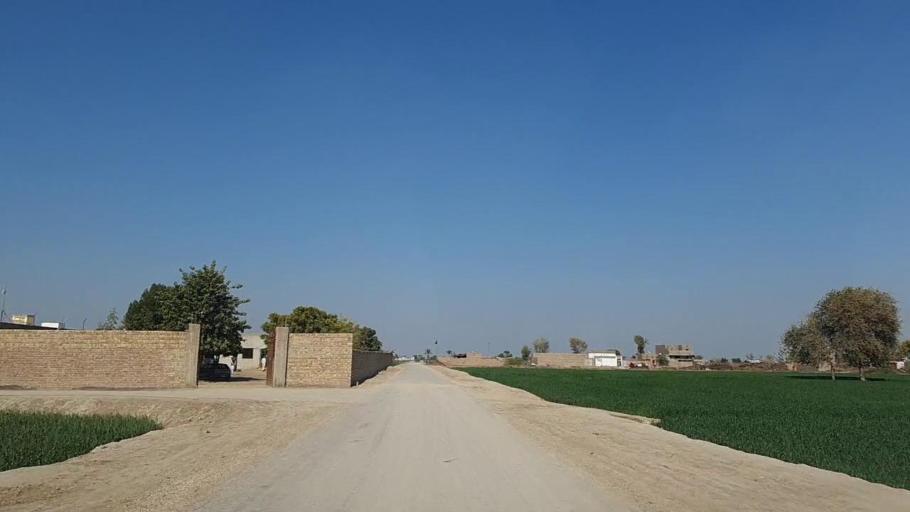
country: PK
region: Sindh
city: Nawabshah
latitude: 26.2495
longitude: 68.4513
